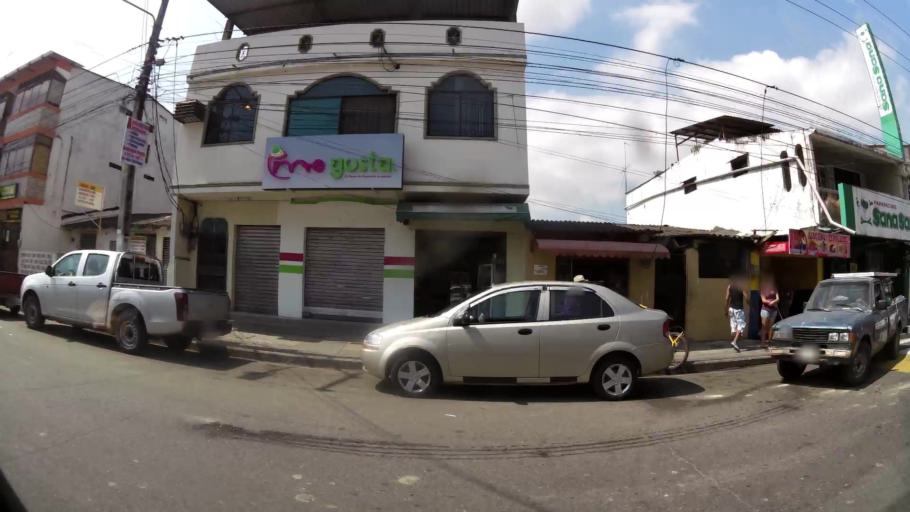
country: EC
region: Guayas
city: Eloy Alfaro
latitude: -2.1635
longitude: -79.8436
